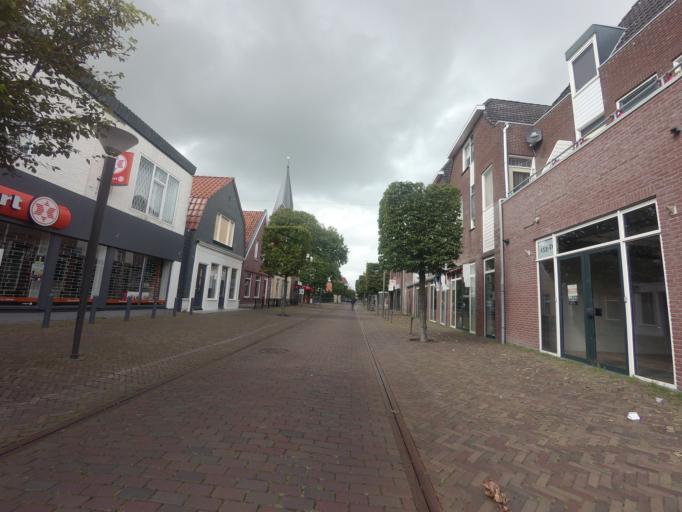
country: NL
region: Friesland
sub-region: Gemeente Skarsterlan
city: Joure
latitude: 52.9661
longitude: 5.7983
